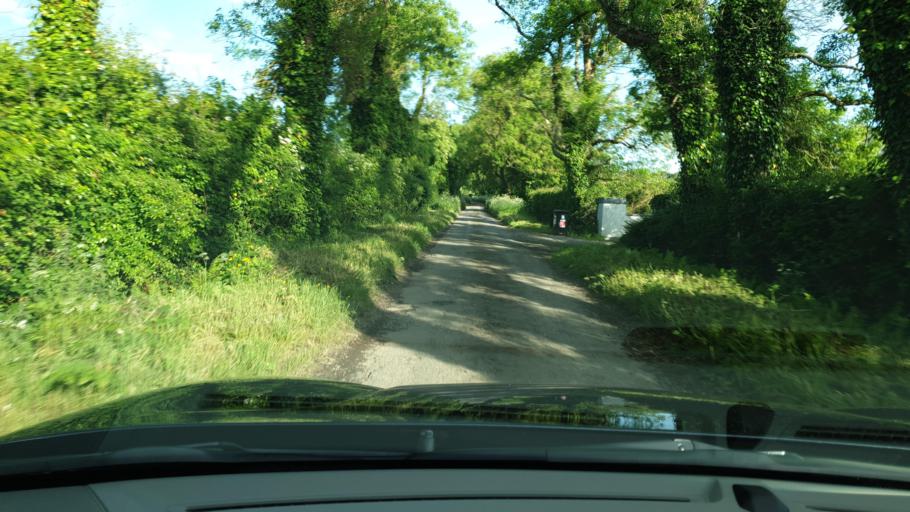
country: IE
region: Leinster
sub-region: An Mhi
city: Ashbourne
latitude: 53.5531
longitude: -6.4248
